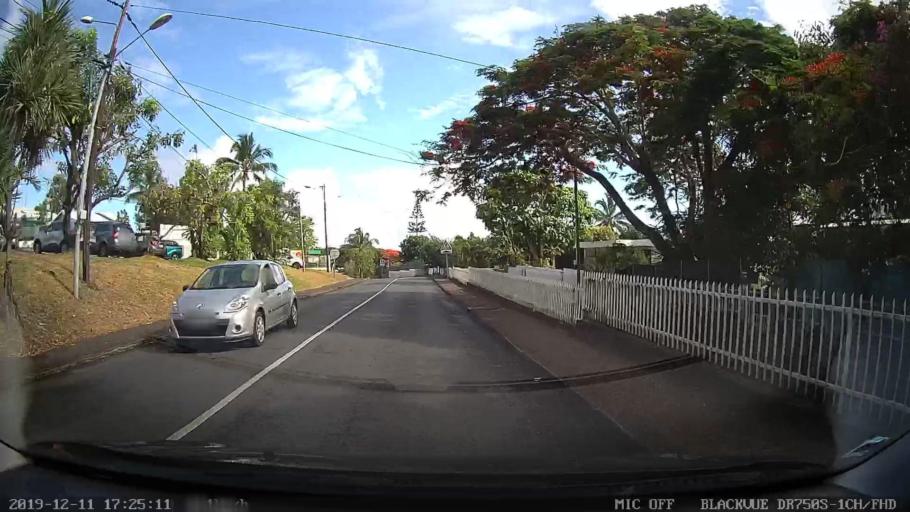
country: RE
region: Reunion
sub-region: Reunion
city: Sainte-Marie
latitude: -20.9106
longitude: 55.5049
